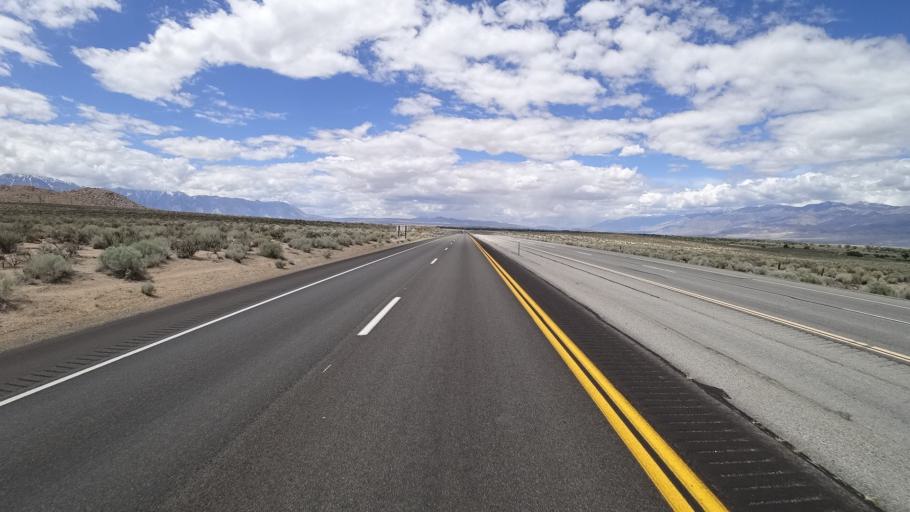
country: US
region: California
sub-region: Inyo County
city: Bishop
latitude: 37.3102
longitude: -118.3835
